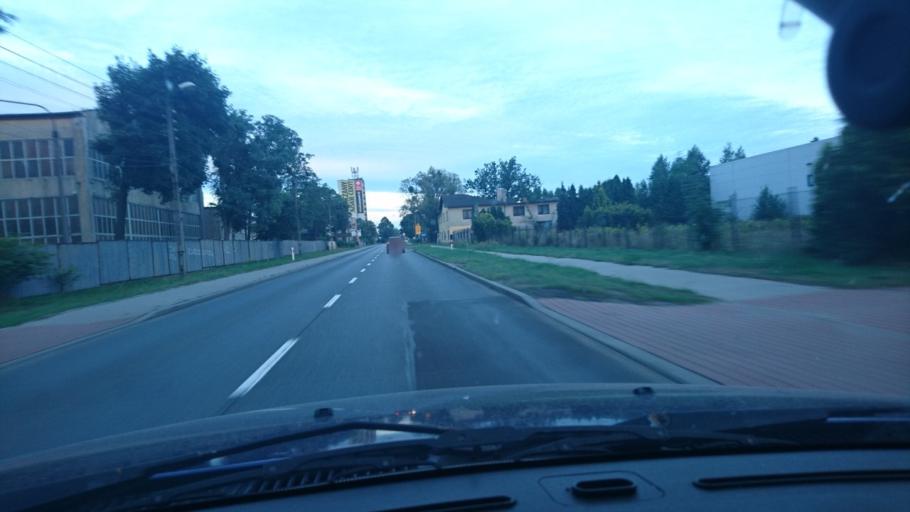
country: PL
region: Silesian Voivodeship
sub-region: Powiat tarnogorski
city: Zbroslawice
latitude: 50.4780
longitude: 18.7945
